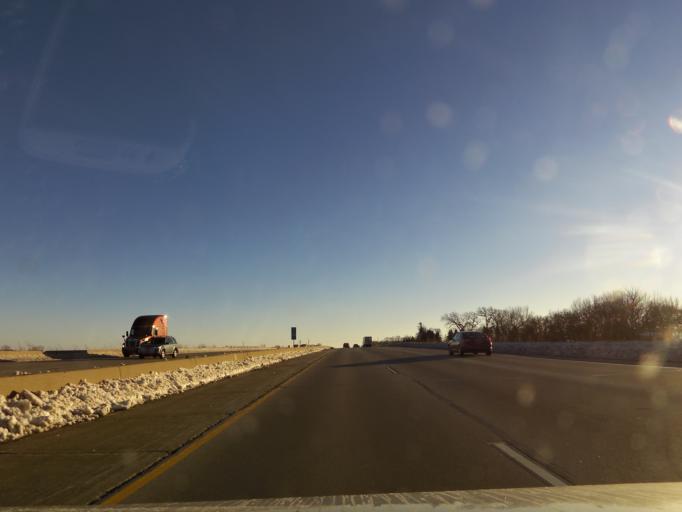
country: US
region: Wisconsin
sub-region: Kenosha County
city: Somers
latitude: 42.6415
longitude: -87.9528
